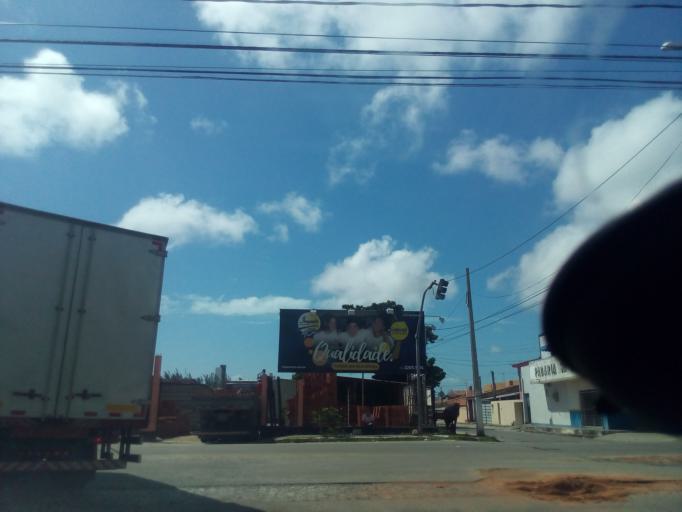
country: BR
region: Rio Grande do Norte
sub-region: Natal
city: Natal
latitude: -5.8247
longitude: -35.2343
